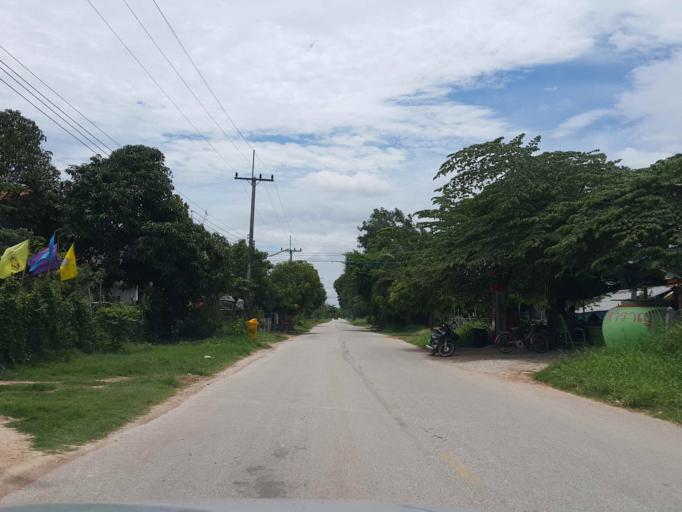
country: TH
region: Sukhothai
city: Ban Na
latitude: 17.0070
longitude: 99.7063
